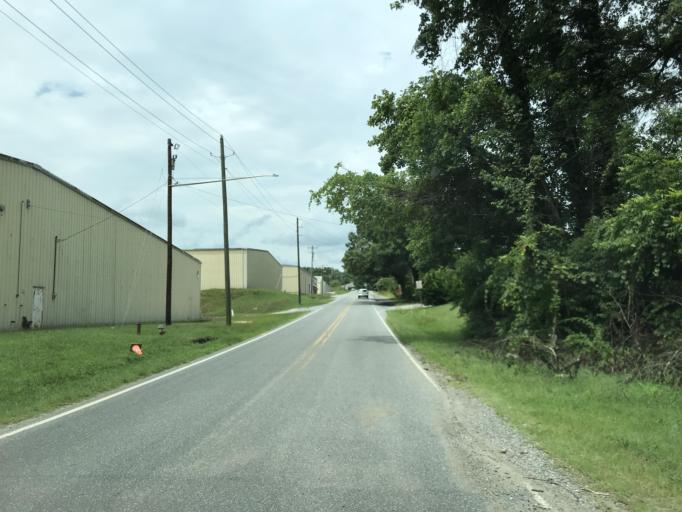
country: US
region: North Carolina
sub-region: Lincoln County
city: Lincolnton
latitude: 35.4855
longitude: -81.2517
